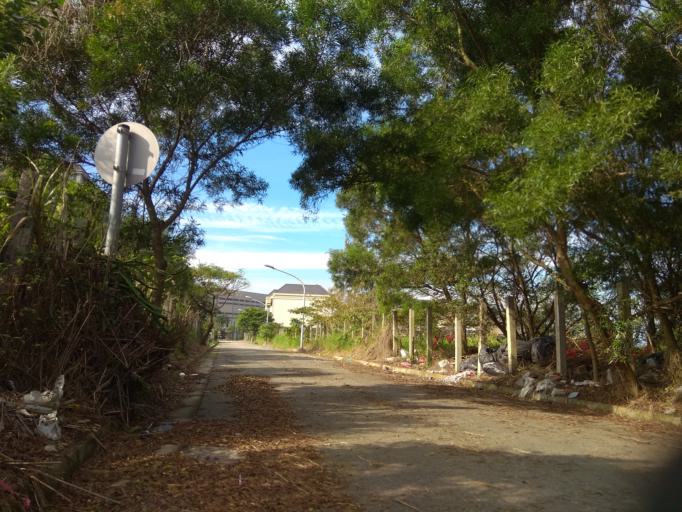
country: TW
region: Taiwan
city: Taoyuan City
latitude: 25.0538
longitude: 121.1798
